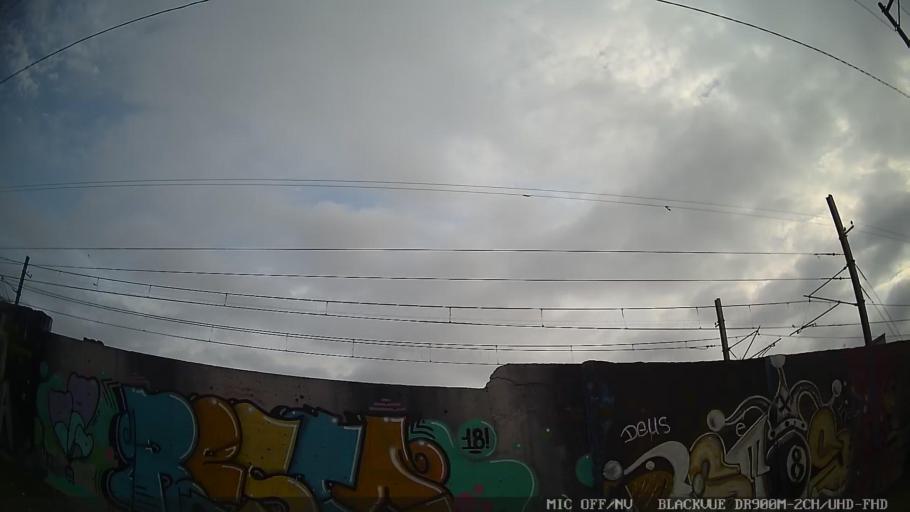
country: BR
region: Sao Paulo
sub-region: Itaquaquecetuba
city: Itaquaquecetuba
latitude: -23.4936
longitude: -46.4109
